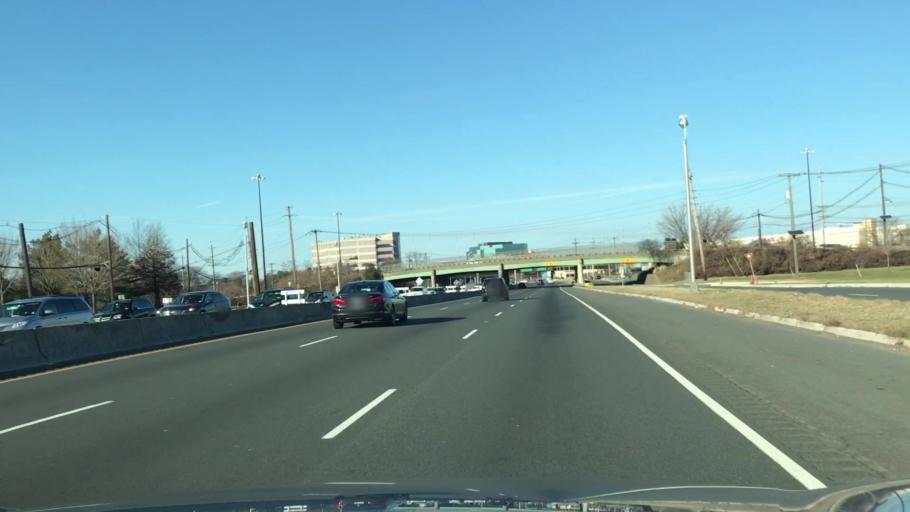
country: US
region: New Jersey
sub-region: Hudson County
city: Secaucus
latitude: 40.7818
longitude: -74.0468
